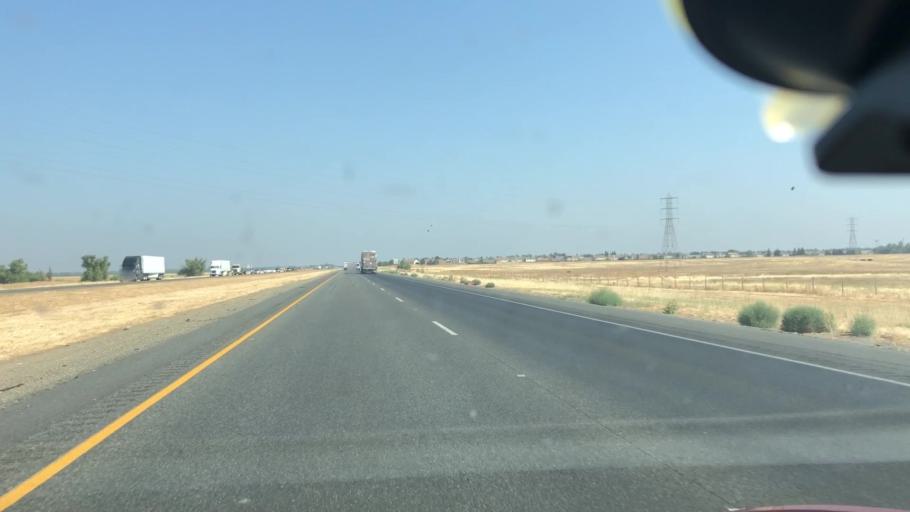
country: US
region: California
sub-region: Sacramento County
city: Laguna
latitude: 38.3852
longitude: -121.4786
